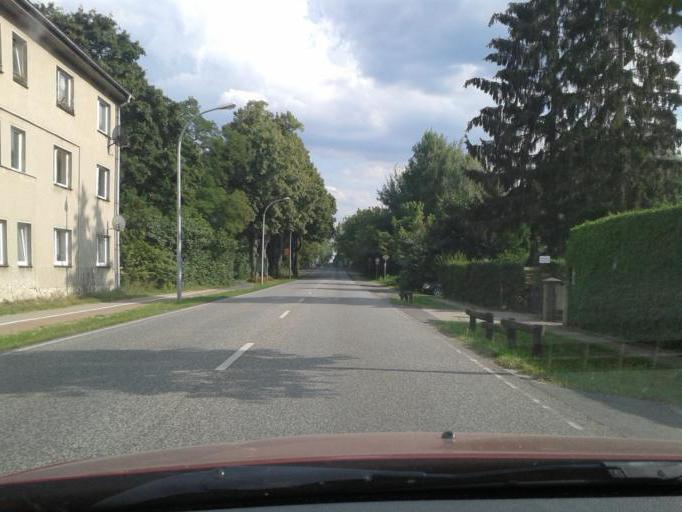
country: DE
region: Brandenburg
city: Oranienburg
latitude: 52.7247
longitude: 13.2491
